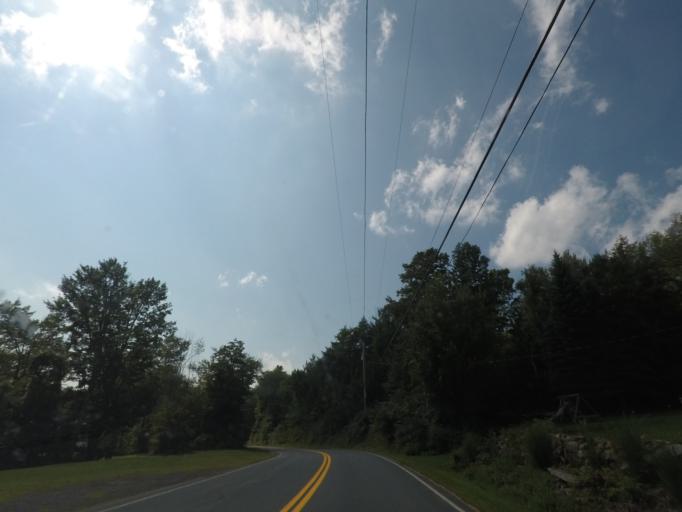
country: US
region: New York
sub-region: Rensselaer County
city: Poestenkill
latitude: 42.6884
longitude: -73.5211
